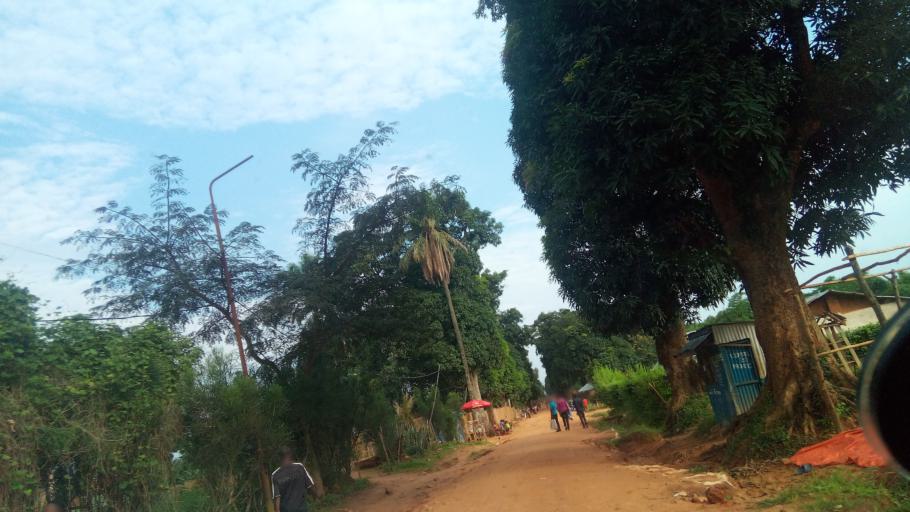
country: CD
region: Kasai-Oriental
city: Kabinda
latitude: -6.1317
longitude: 24.4846
